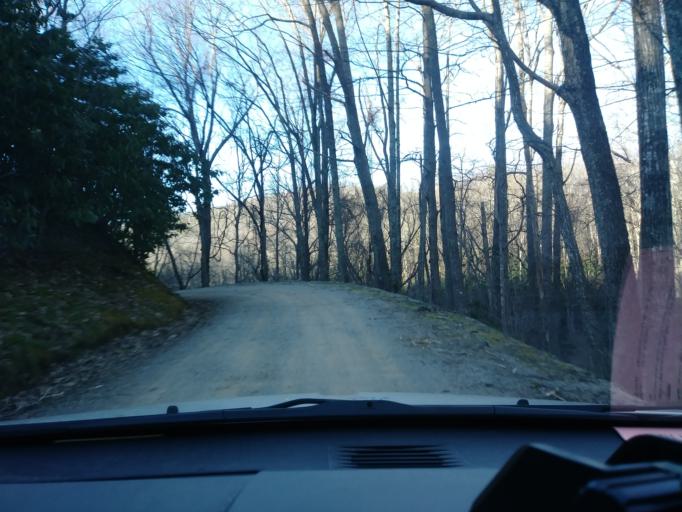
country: US
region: Tennessee
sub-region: Greene County
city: Tusculum
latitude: 36.0655
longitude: -82.6805
